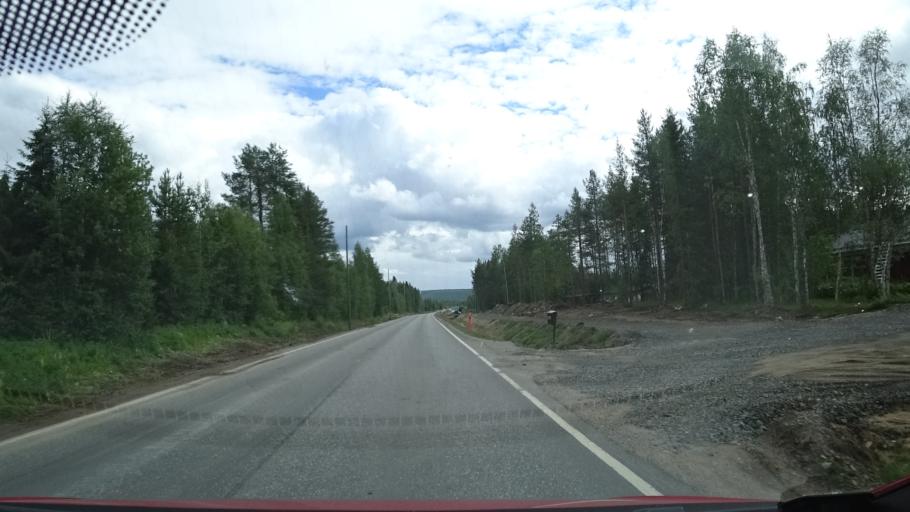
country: FI
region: Lapland
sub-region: Rovaniemi
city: Rovaniemi
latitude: 66.5337
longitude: 25.7322
